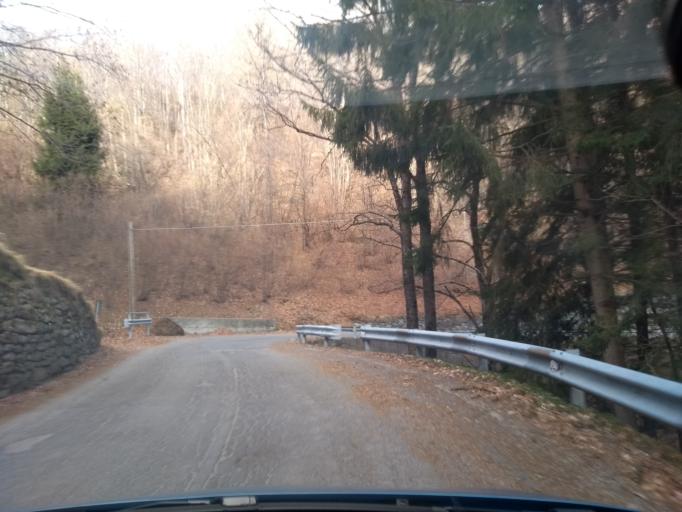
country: IT
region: Piedmont
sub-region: Provincia di Torino
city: Ala di Stura
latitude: 45.3151
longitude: 7.2809
